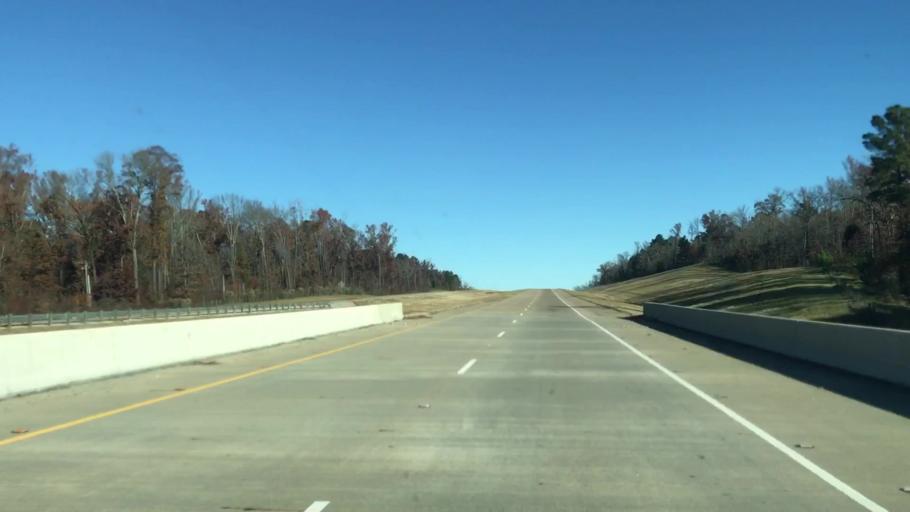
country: US
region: Louisiana
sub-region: Caddo Parish
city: Oil City
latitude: 32.7886
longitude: -93.8880
